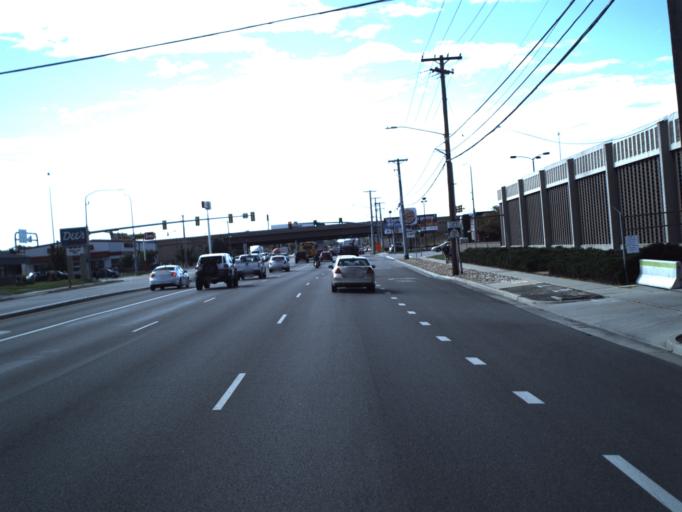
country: US
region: Utah
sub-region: Salt Lake County
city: South Salt Lake
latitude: 40.7272
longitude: -111.9392
